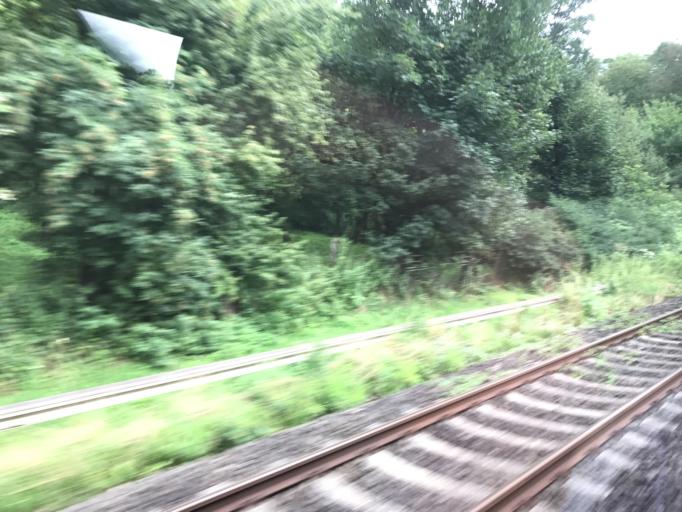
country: DE
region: Hesse
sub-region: Regierungsbezirk Giessen
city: Runkel
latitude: 50.3999
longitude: 8.1674
